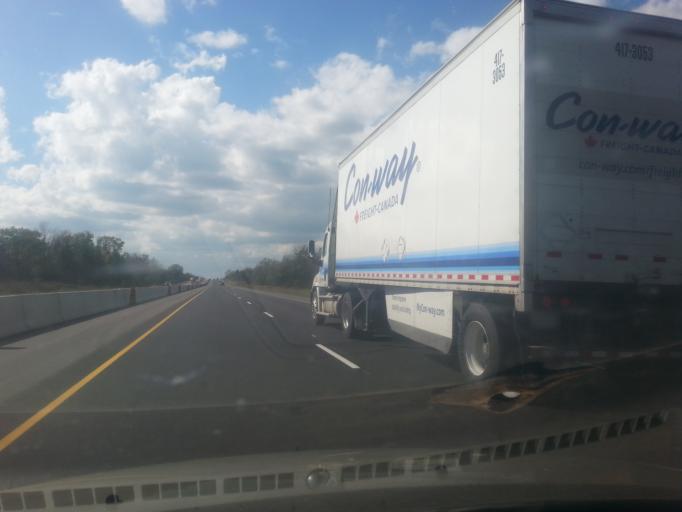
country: CA
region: Ontario
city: Deseronto
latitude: 44.2271
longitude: -77.1894
